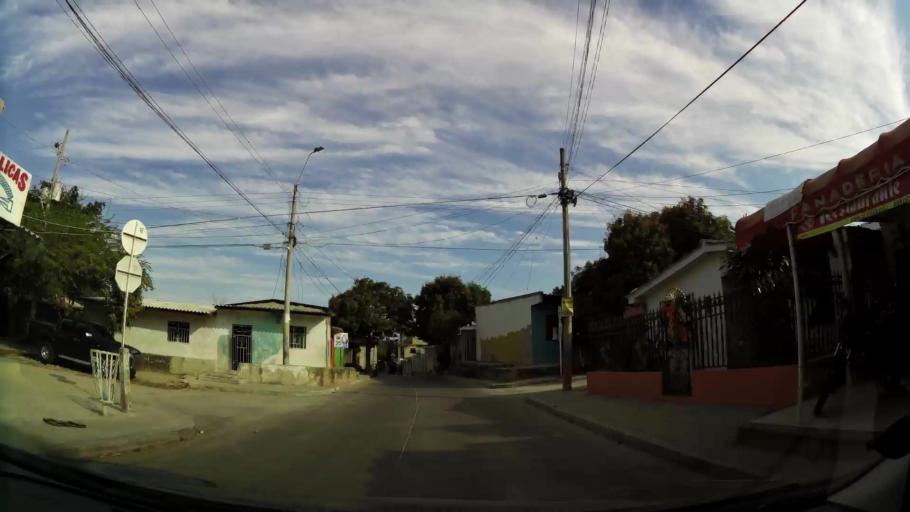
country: CO
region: Atlantico
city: Soledad
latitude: 10.9245
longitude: -74.8133
